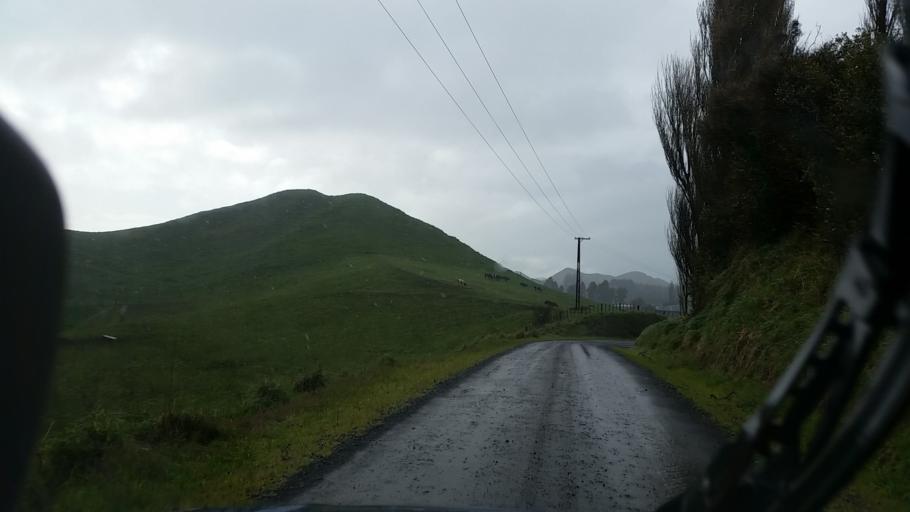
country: NZ
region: Taranaki
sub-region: South Taranaki District
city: Eltham
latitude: -39.3494
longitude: 174.4361
